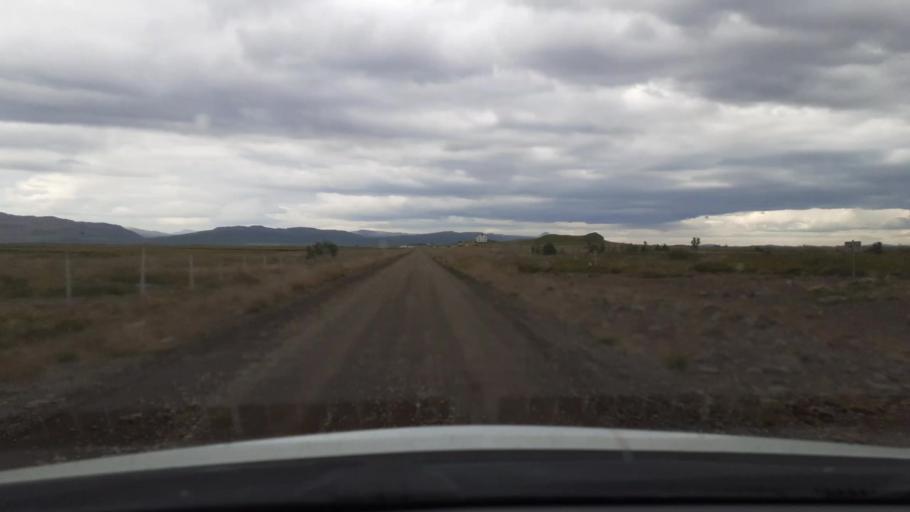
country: IS
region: West
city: Borgarnes
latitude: 64.6477
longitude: -21.8880
